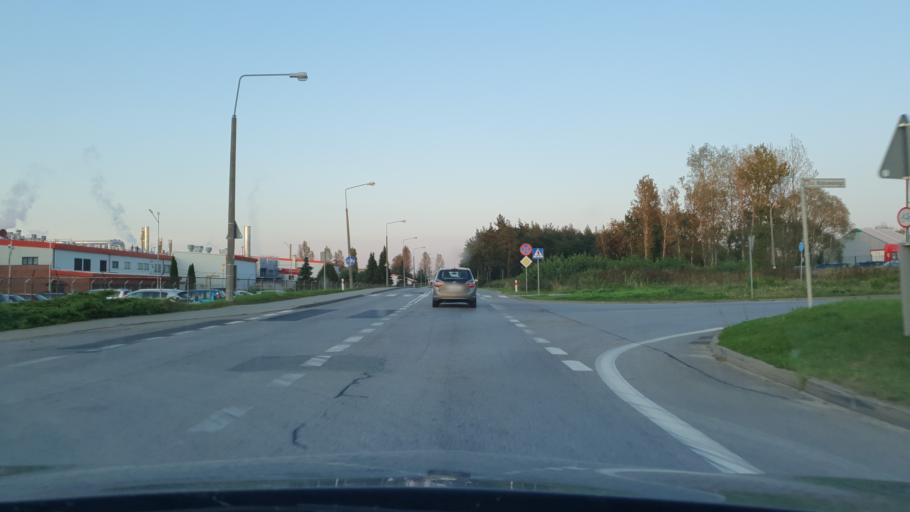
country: PL
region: Pomeranian Voivodeship
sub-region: Powiat leborski
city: Lebork
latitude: 54.5347
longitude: 17.7644
